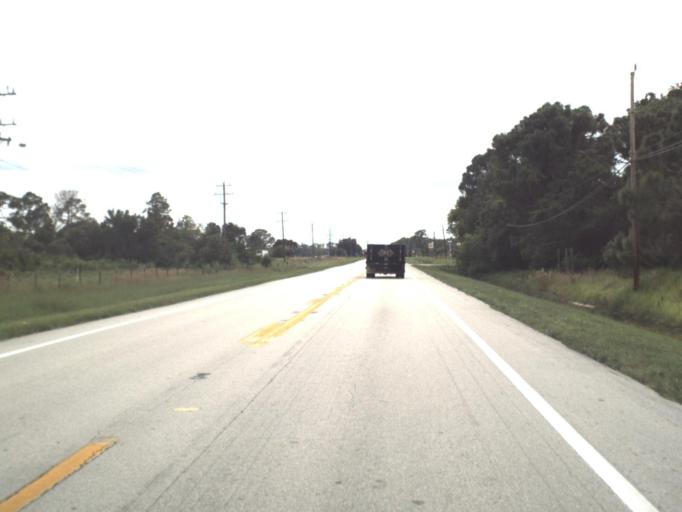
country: US
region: Florida
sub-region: Lee County
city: Fort Myers Shores
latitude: 26.7453
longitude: -81.7610
